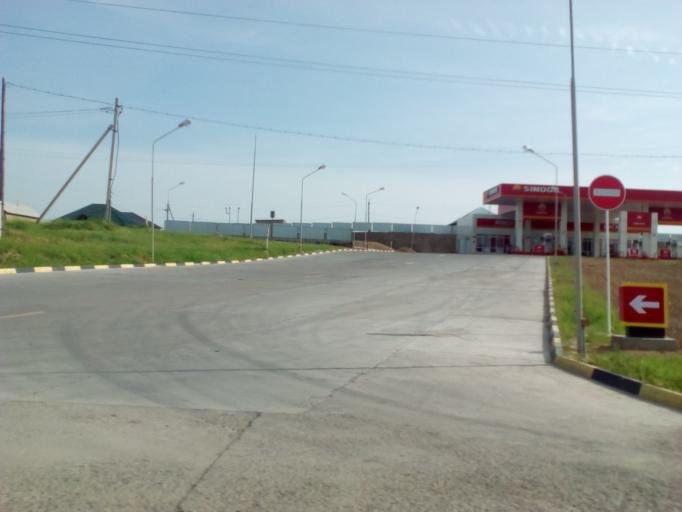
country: KZ
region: Ongtustik Qazaqstan
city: Shymkent
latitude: 42.3862
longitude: 69.4765
